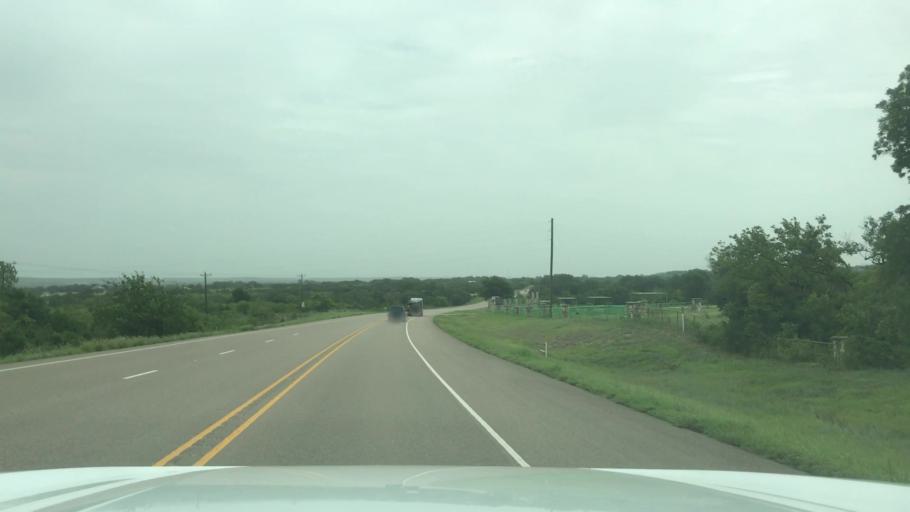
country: US
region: Texas
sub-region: Bosque County
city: Meridian
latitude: 31.9443
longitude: -97.7184
